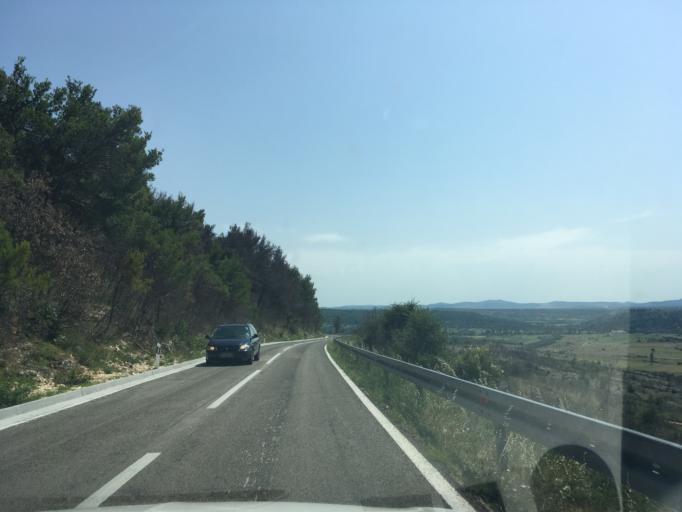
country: HR
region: Sibensko-Kniniska
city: Kistanje
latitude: 43.9444
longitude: 15.8334
